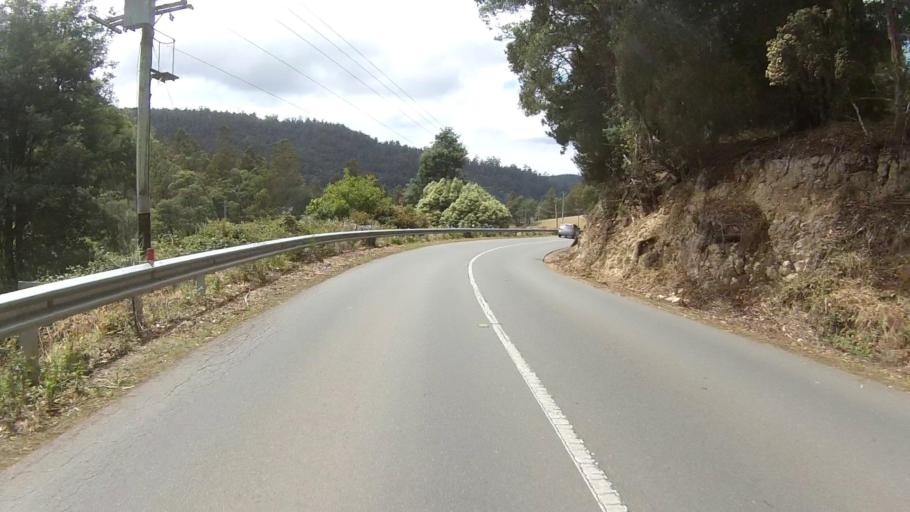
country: AU
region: Tasmania
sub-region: Kingborough
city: Kettering
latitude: -43.1063
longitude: 147.2039
